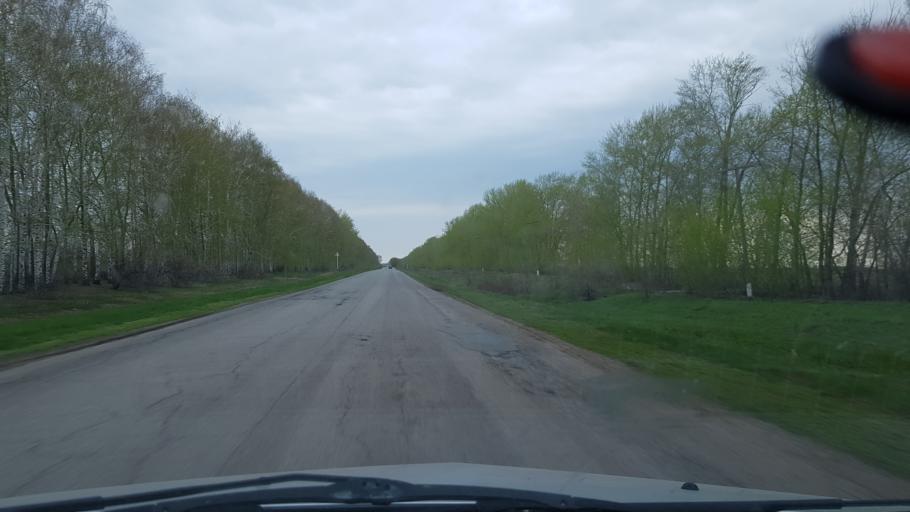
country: RU
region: Samara
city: Podstepki
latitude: 53.6637
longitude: 49.1869
